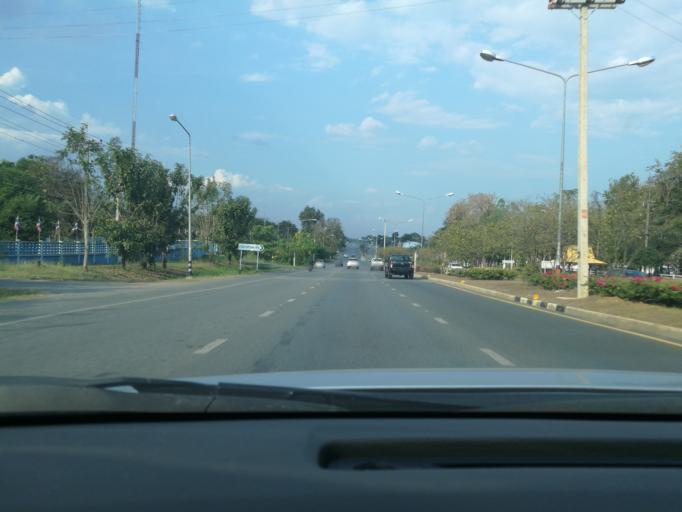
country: TH
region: Phetchabun
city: Phetchabun
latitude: 16.4552
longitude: 101.1544
